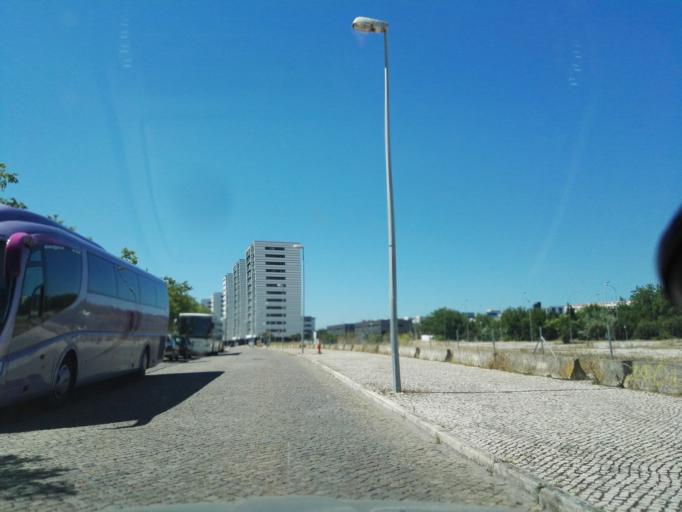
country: PT
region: Lisbon
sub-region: Loures
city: Sacavem
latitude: 38.7949
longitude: -9.0972
